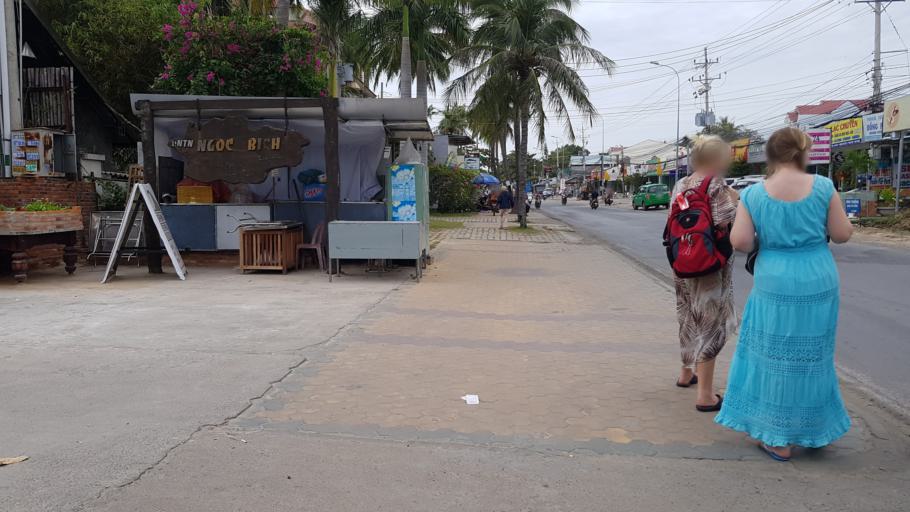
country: VN
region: Binh Thuan
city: Phan Thiet
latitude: 10.9474
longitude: 108.2016
